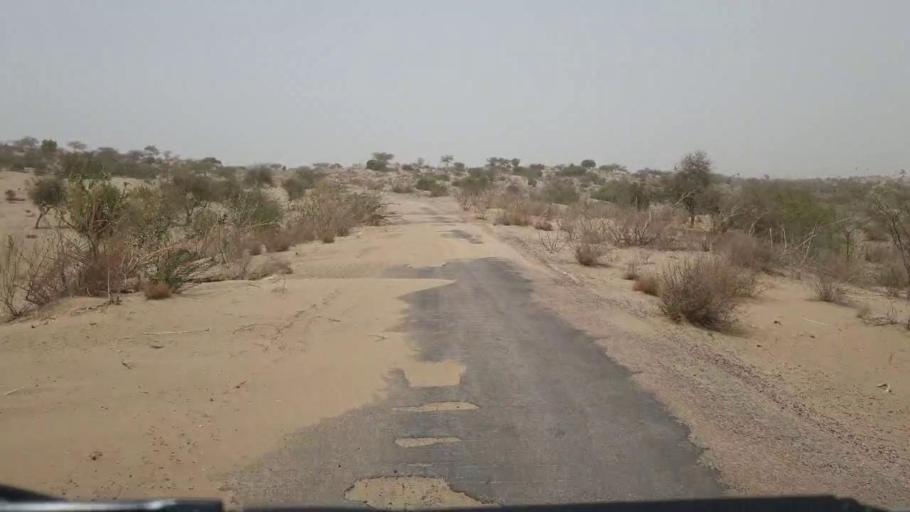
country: PK
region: Sindh
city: Naukot
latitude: 24.7772
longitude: 69.5366
